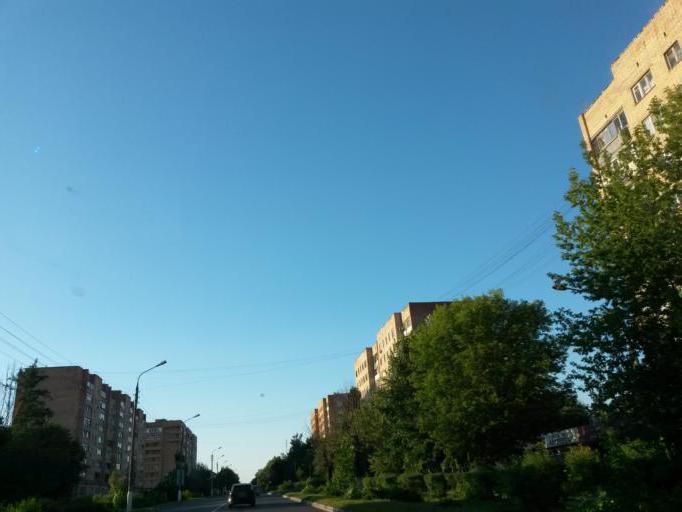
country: RU
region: Moskovskaya
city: Serpukhov
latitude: 54.9256
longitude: 37.4031
